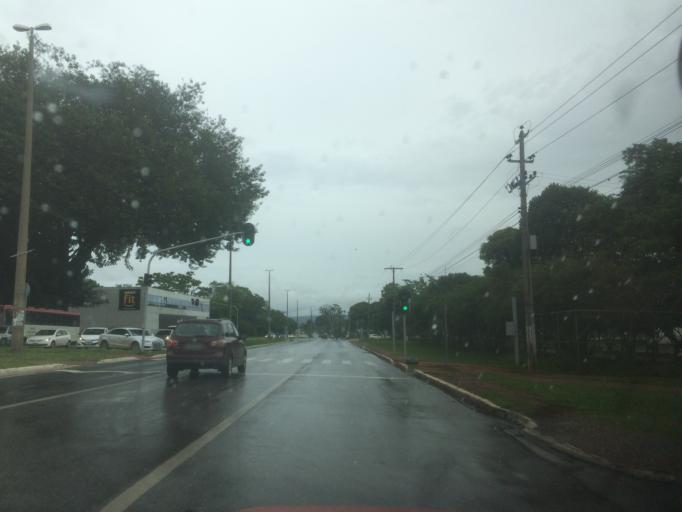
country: BR
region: Federal District
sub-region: Brasilia
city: Brasilia
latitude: -15.7672
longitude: -47.8757
